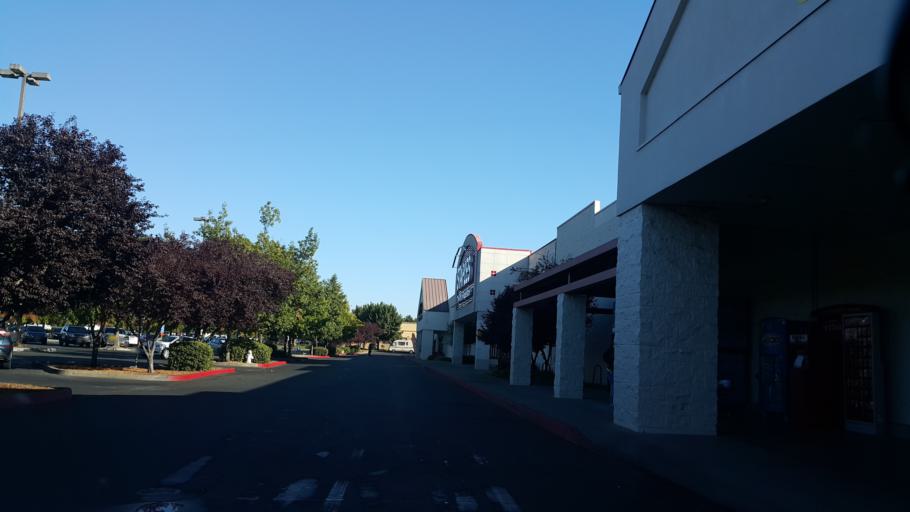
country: US
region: California
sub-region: Mendocino County
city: Ukiah
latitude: 39.1312
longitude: -123.1971
